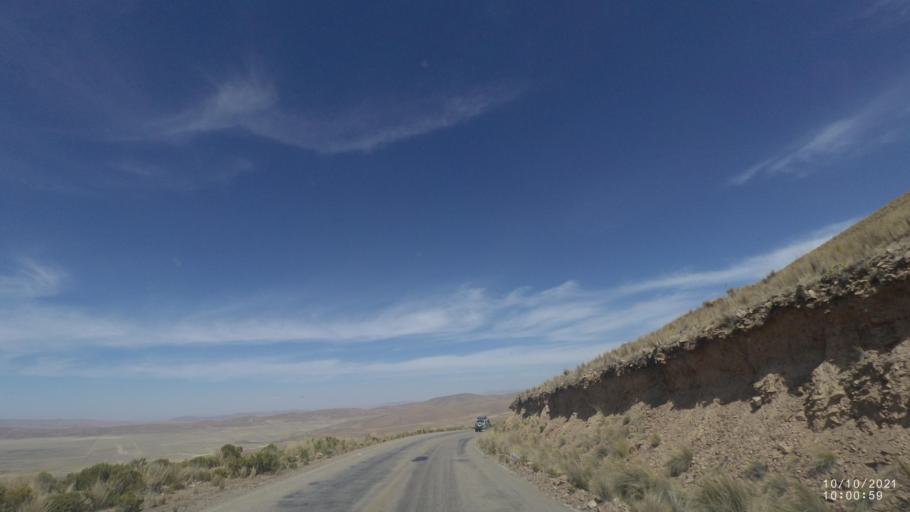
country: BO
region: La Paz
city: Eucaliptus
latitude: -17.3670
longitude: -67.4174
